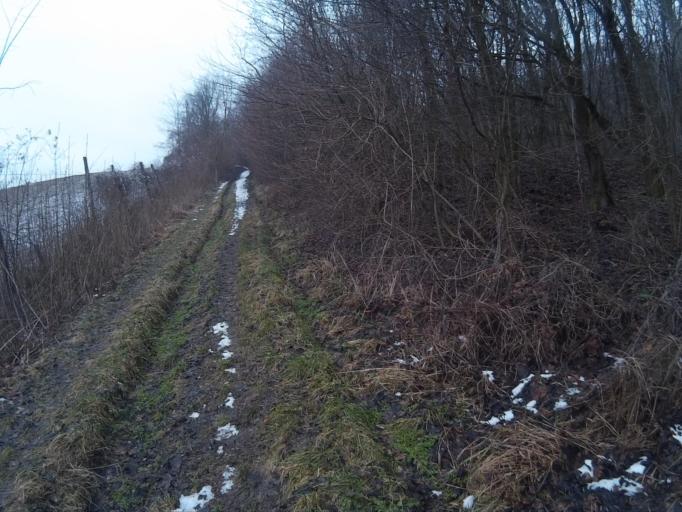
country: HU
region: Komarom-Esztergom
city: Tarjan
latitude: 47.5980
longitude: 18.5126
